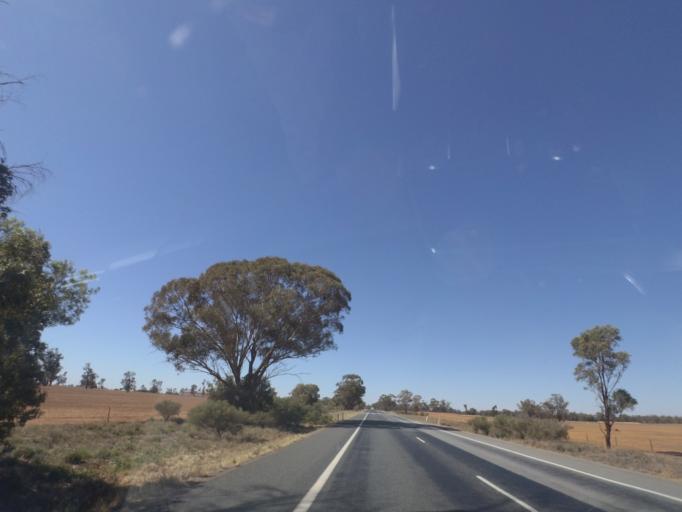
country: AU
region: New South Wales
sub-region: Bland
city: West Wyalong
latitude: -34.1885
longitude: 147.1121
